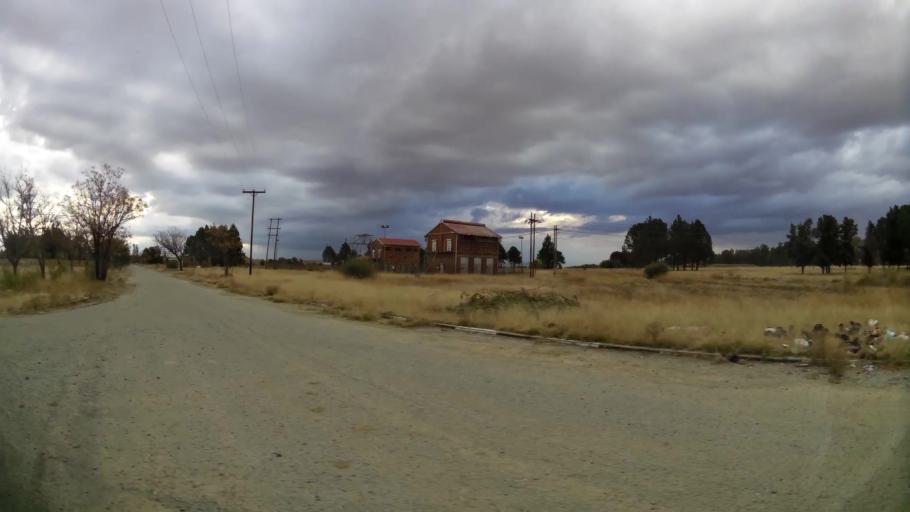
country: ZA
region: Orange Free State
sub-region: Lejweleputswa District Municipality
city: Welkom
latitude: -27.9675
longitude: 26.7012
